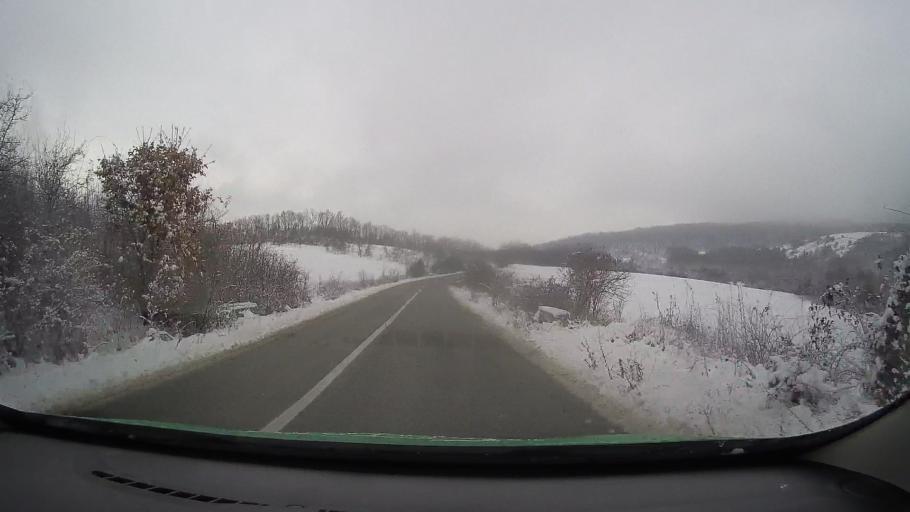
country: RO
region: Hunedoara
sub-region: Oras Hateg
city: Hateg
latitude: 45.6418
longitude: 22.9184
